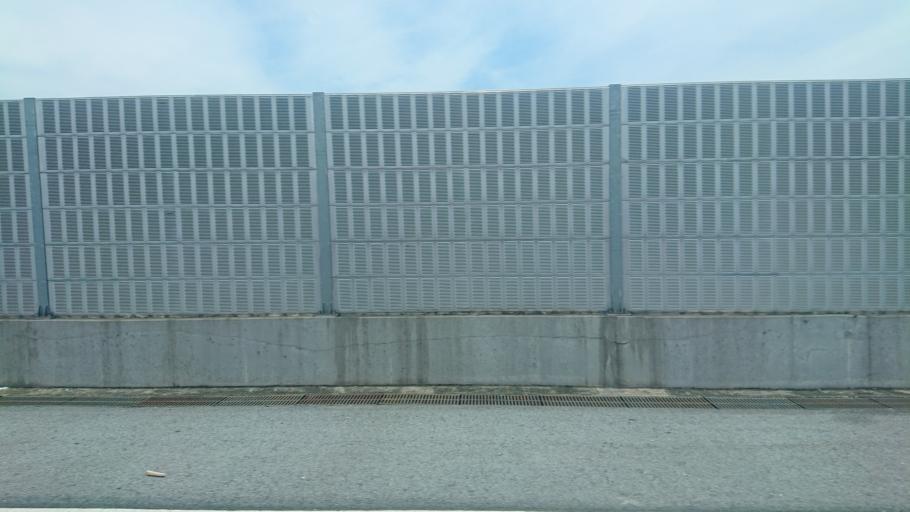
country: VN
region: Hai Duong
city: Tu Ky
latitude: 20.8356
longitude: 106.4345
